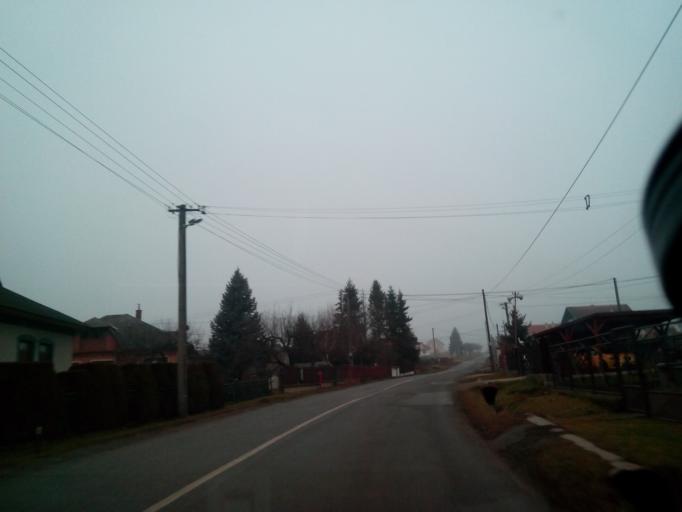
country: SK
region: Kosicky
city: Krompachy
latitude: 48.9755
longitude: 20.9473
